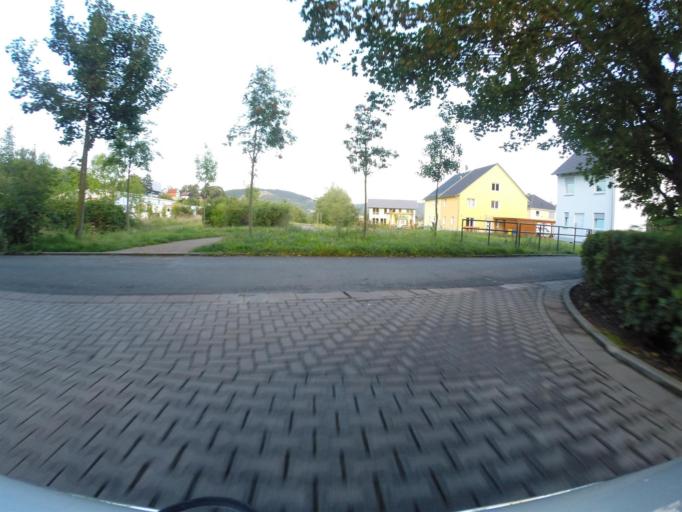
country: DE
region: Thuringia
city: Jena
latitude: 50.9065
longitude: 11.5675
